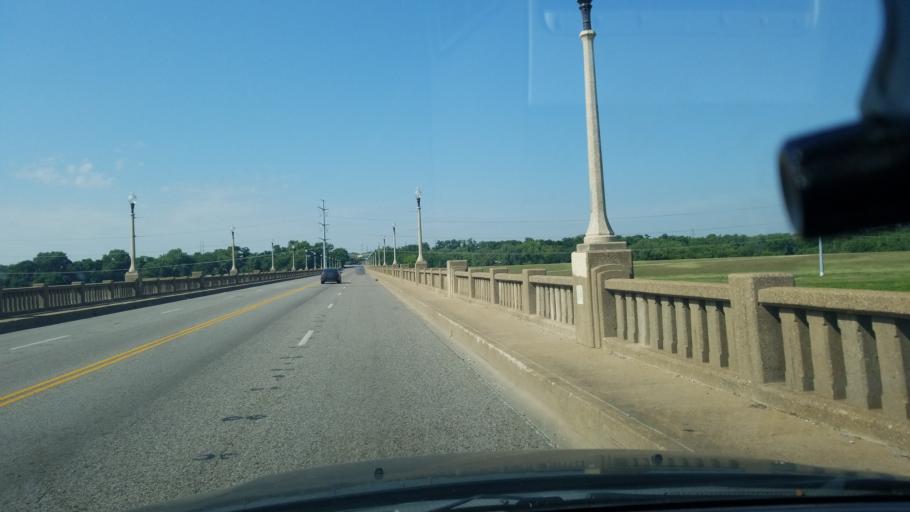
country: US
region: Texas
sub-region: Dallas County
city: Dallas
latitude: 32.7545
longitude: -96.7966
